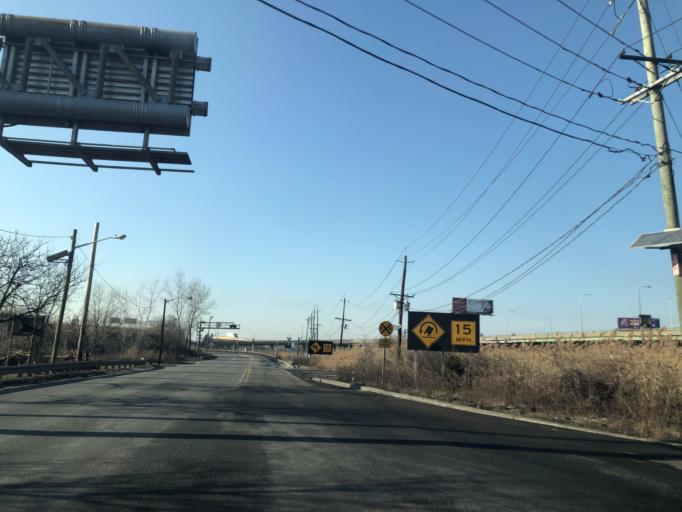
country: US
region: New Jersey
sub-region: Essex County
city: Newark
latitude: 40.7042
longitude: -74.1477
